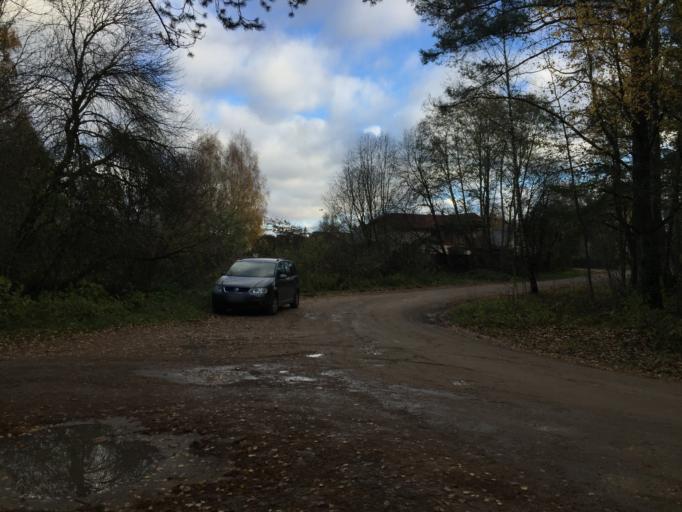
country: LV
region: Carnikava
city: Carnikava
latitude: 57.1448
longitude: 24.2639
